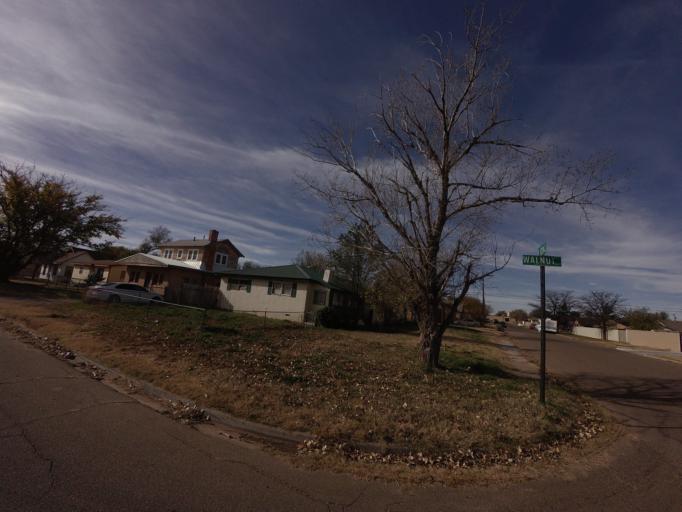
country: US
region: New Mexico
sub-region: Curry County
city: Clovis
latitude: 34.4099
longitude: -103.1890
